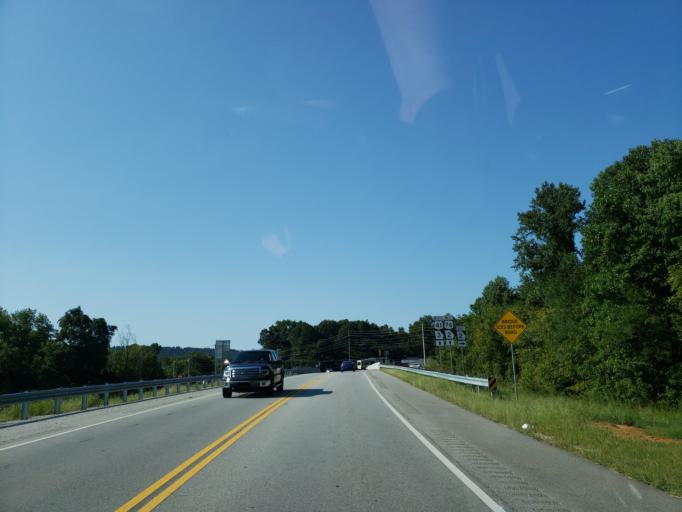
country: US
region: Georgia
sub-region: Catoosa County
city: Ringgold
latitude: 34.9044
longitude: -85.0769
